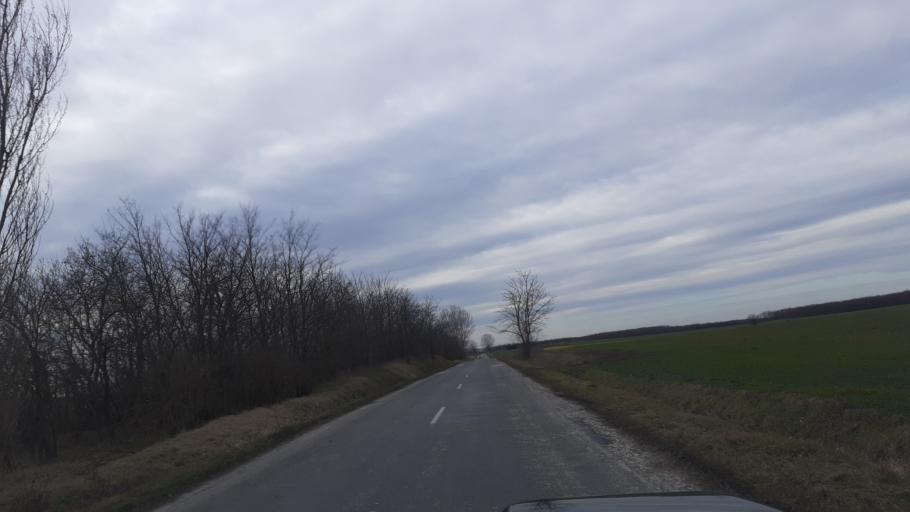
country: HU
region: Fejer
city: Sarbogard
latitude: 46.9078
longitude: 18.5837
